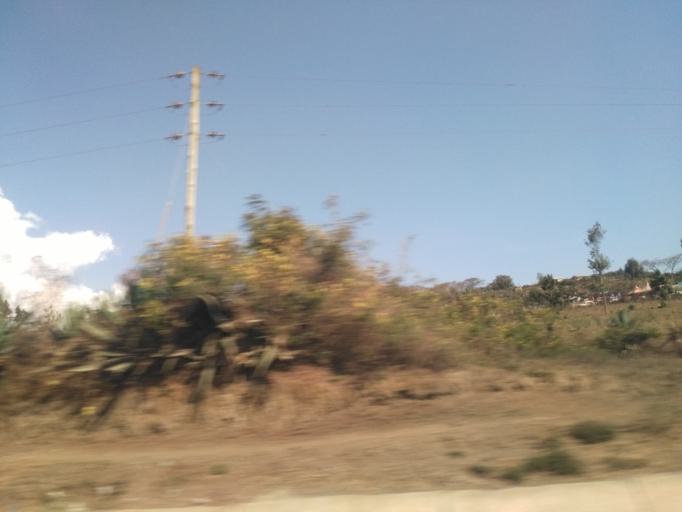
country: TZ
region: Arusha
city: Arusha
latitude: -3.2186
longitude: 36.6070
